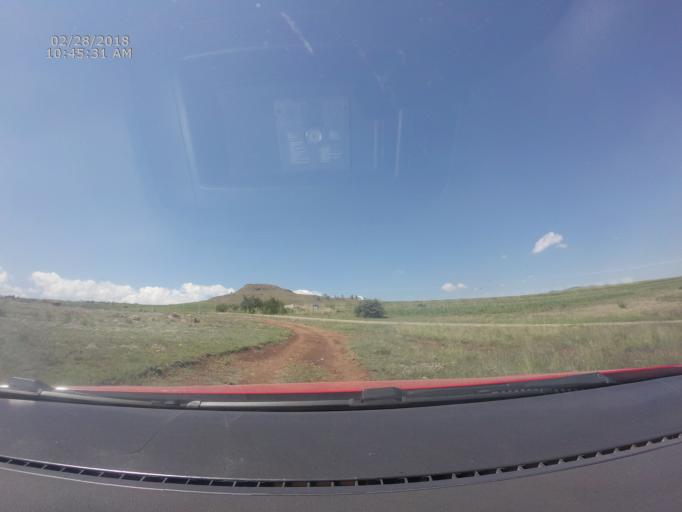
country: LS
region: Berea
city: Teyateyaneng
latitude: -29.2131
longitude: 27.8618
